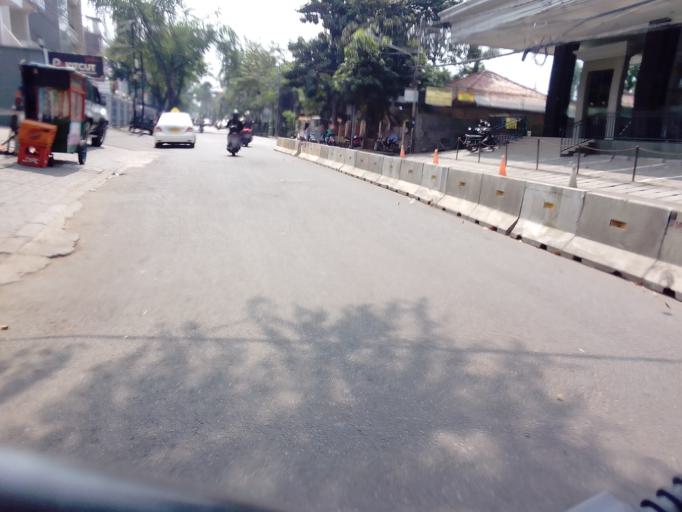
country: ID
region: Jakarta Raya
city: Jakarta
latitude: -6.2088
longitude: 106.8119
